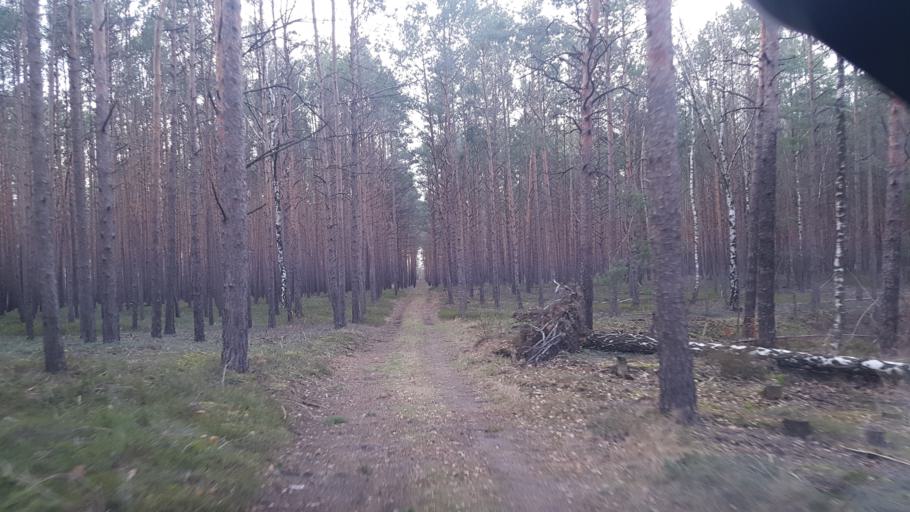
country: DE
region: Brandenburg
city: Schonborn
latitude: 51.5927
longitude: 13.4739
